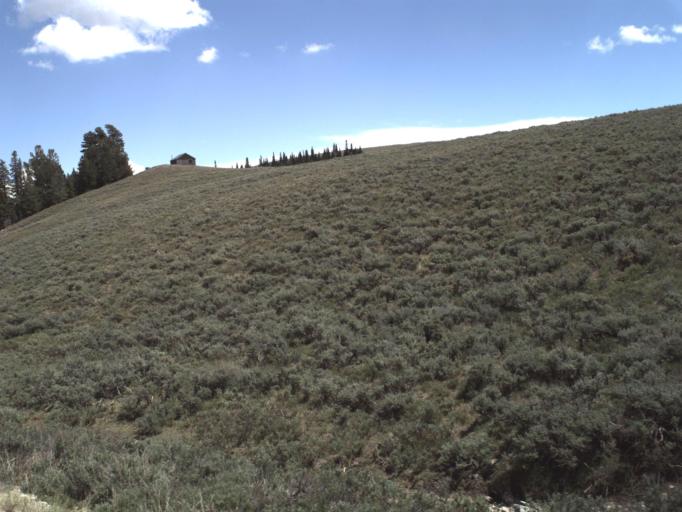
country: US
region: Utah
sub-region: Rich County
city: Randolph
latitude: 41.4837
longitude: -111.4122
